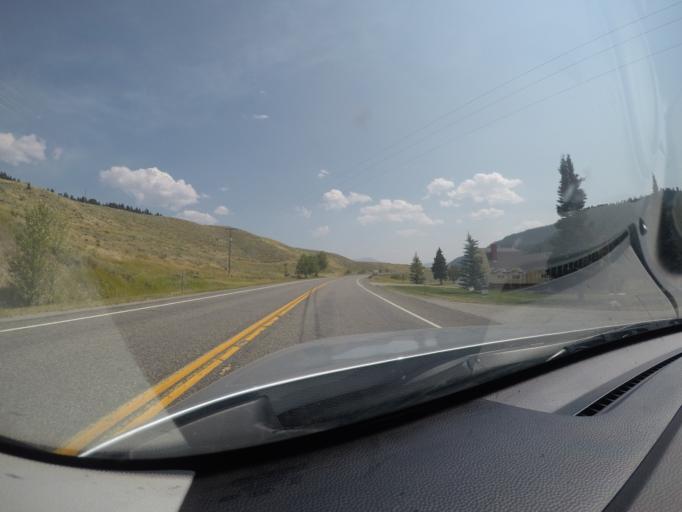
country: US
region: Montana
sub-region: Gallatin County
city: Big Sky
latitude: 44.8804
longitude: -111.5693
